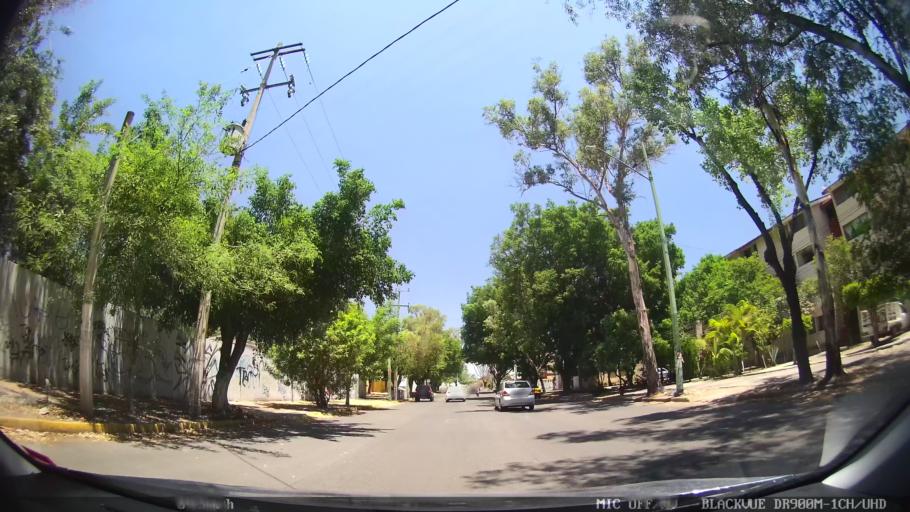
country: MX
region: Jalisco
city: Tlaquepaque
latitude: 20.6604
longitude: -103.2783
